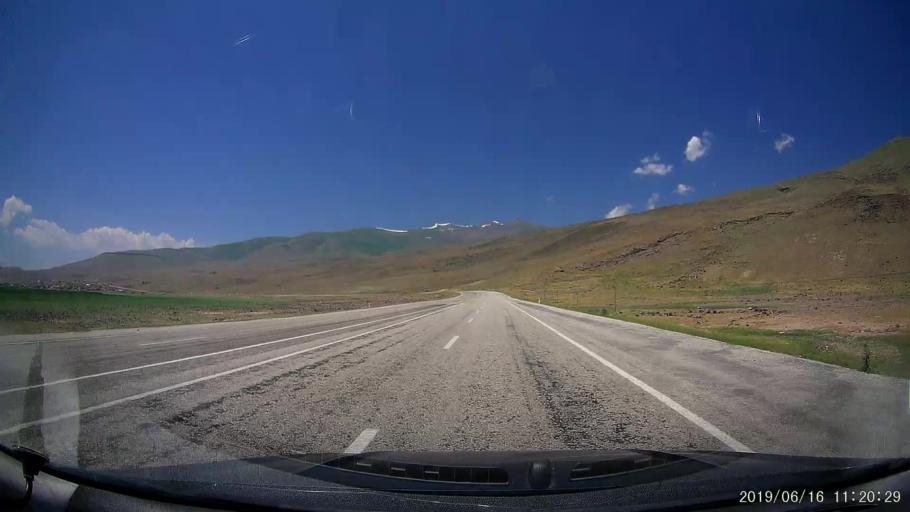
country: TR
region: Agri
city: Dogubayazit
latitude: 39.6992
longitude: 44.0892
